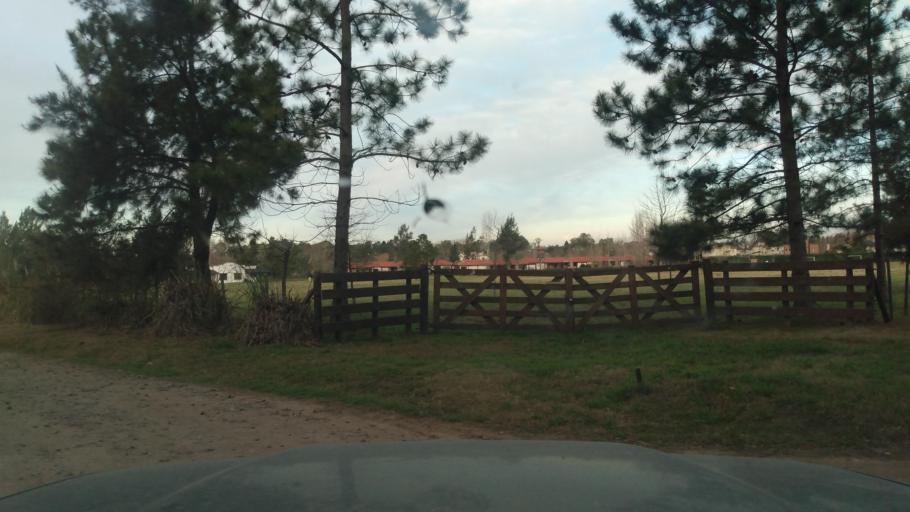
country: AR
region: Buenos Aires
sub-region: Partido de Lujan
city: Lujan
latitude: -34.5763
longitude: -59.0695
